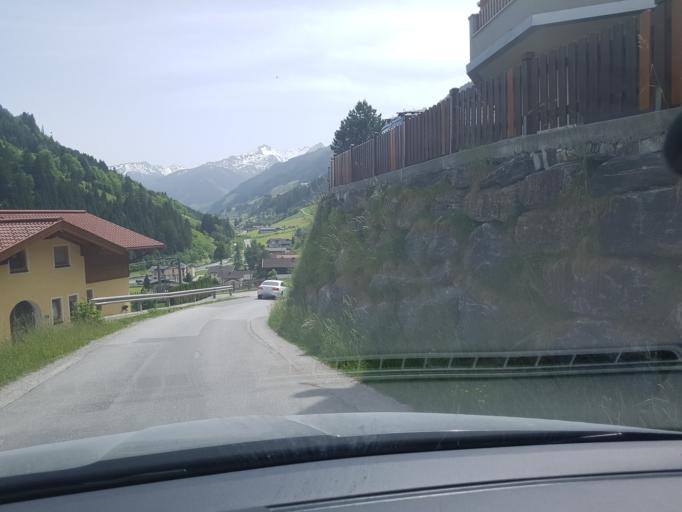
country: AT
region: Salzburg
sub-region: Politischer Bezirk Sankt Johann im Pongau
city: Schwarzach im Pongau
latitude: 47.2681
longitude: 13.2011
